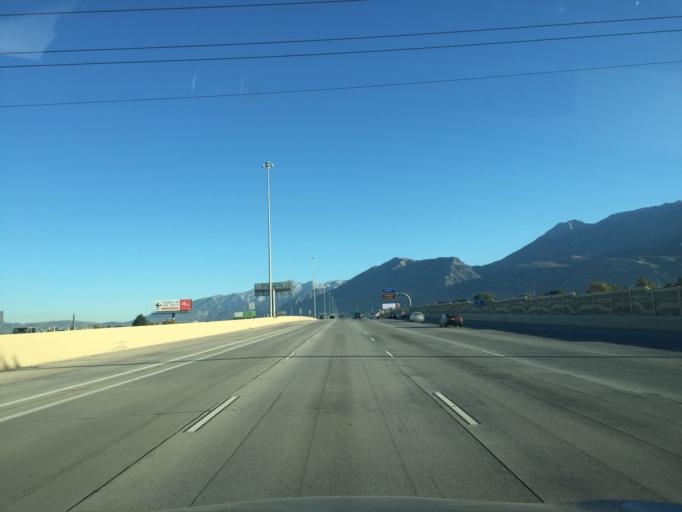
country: US
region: Utah
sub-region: Utah County
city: Orem
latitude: 40.3025
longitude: -111.7257
